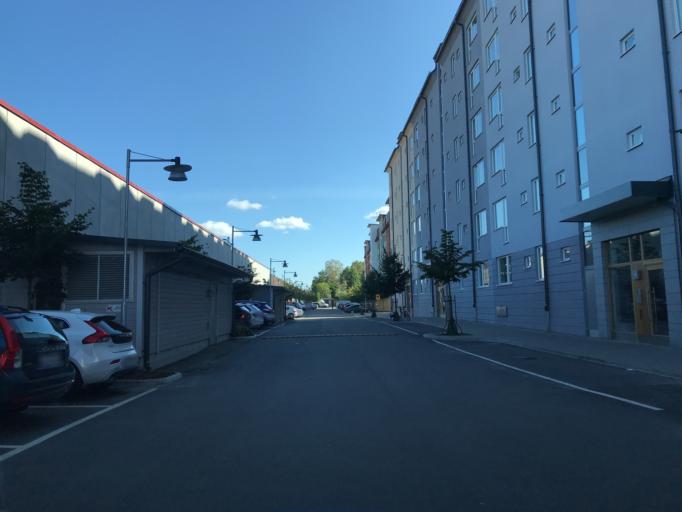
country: SE
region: Stockholm
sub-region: Sollentuna Kommun
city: Sollentuna
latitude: 59.4335
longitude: 17.9428
